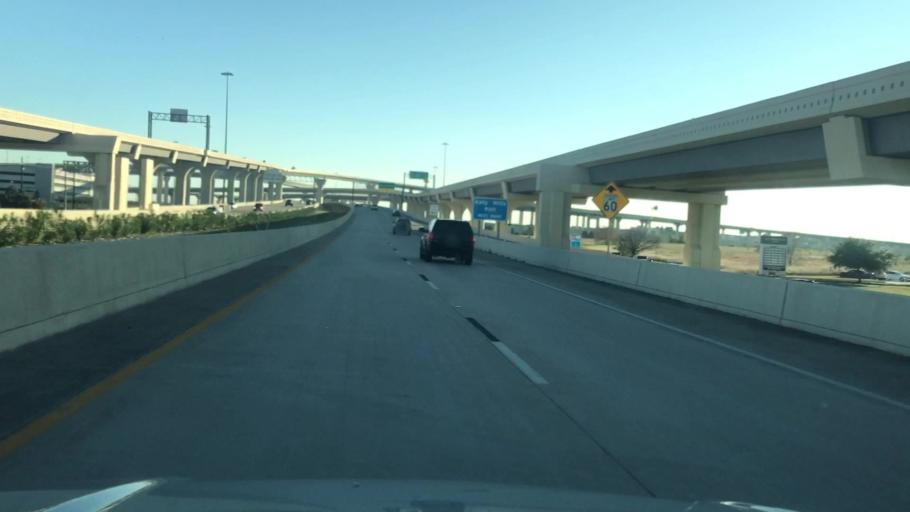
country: US
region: Texas
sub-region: Harris County
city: Katy
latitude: 29.7911
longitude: -95.7769
